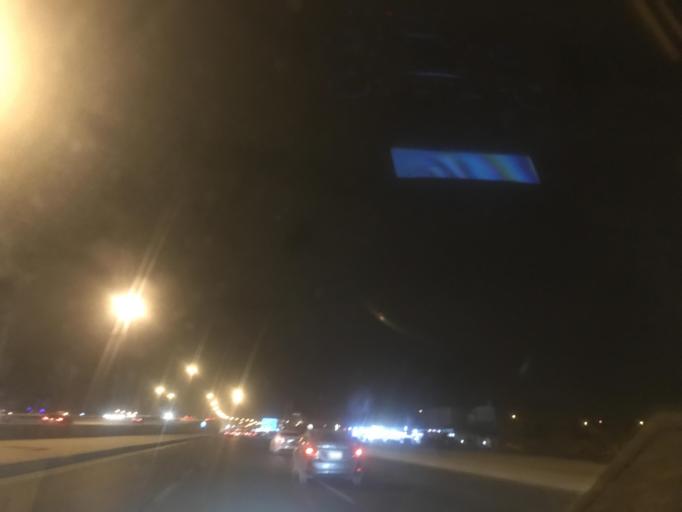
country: SA
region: Ar Riyad
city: Riyadh
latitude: 24.7707
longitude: 46.5748
